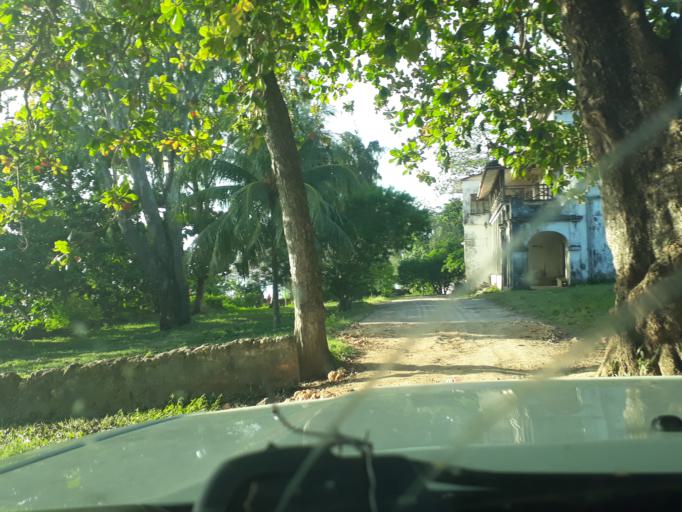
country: TZ
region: Zanzibar North
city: Mkokotoni
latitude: -5.8742
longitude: 39.2575
